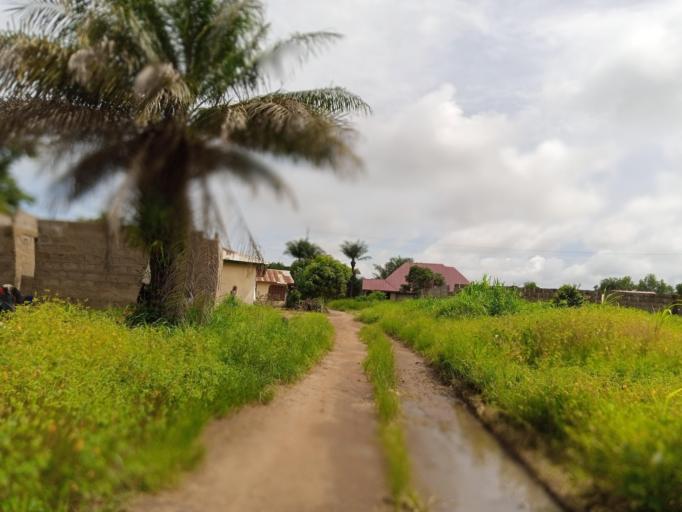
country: SL
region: Northern Province
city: Masoyila
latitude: 8.5907
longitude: -13.1951
